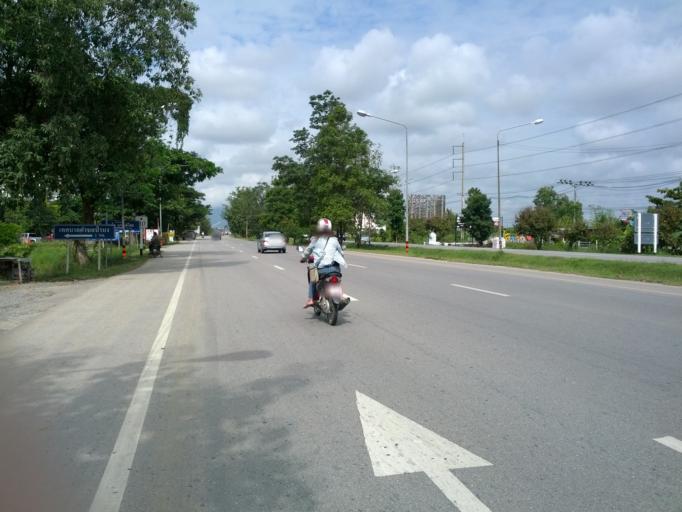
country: TH
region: Chiang Mai
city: Saraphi
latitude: 18.7481
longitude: 99.0674
